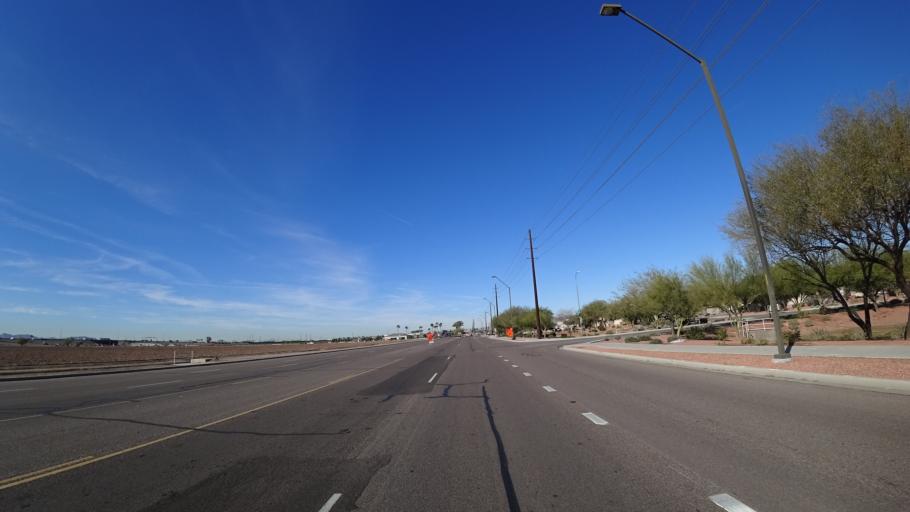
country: US
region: Arizona
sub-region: Maricopa County
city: Tolleson
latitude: 33.4643
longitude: -112.3022
